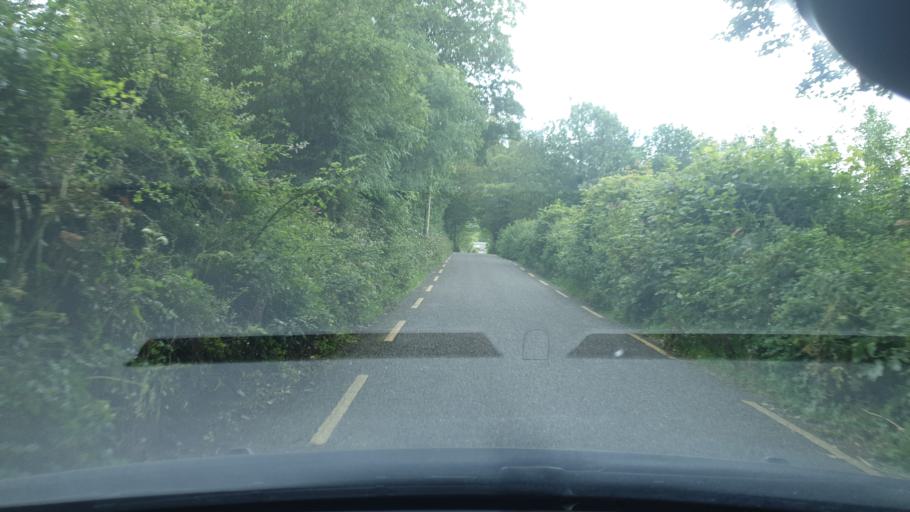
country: IE
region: Munster
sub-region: Ciarrai
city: Tralee
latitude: 52.2470
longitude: -9.6444
